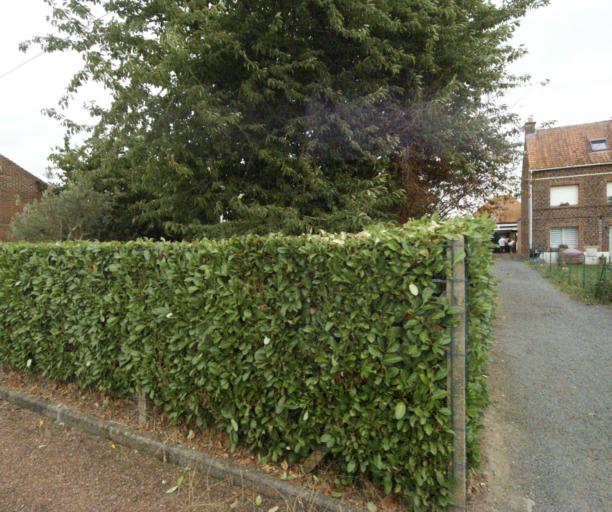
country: FR
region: Nord-Pas-de-Calais
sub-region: Departement du Nord
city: Fretin
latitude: 50.5601
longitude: 3.1567
